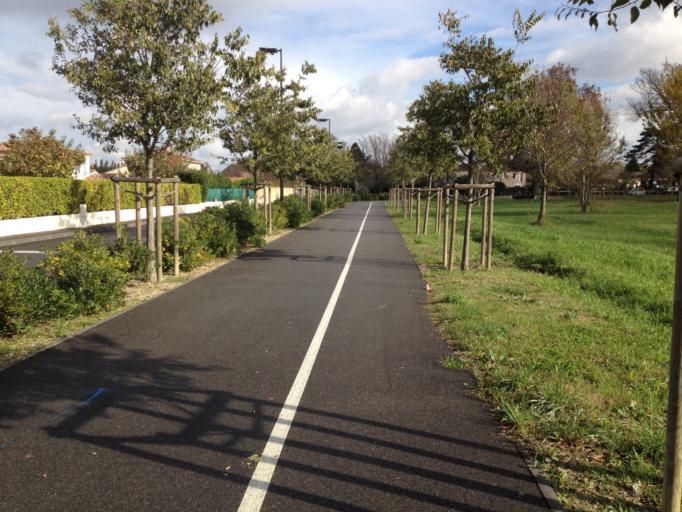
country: FR
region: Provence-Alpes-Cote d'Azur
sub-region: Departement du Vaucluse
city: Orange
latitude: 44.1328
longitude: 4.8244
